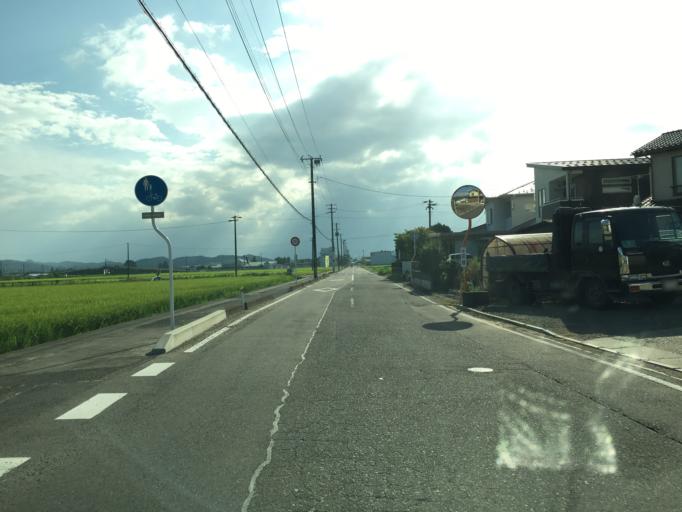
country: JP
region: Fukushima
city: Yanagawamachi-saiwaicho
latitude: 37.8277
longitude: 140.5794
